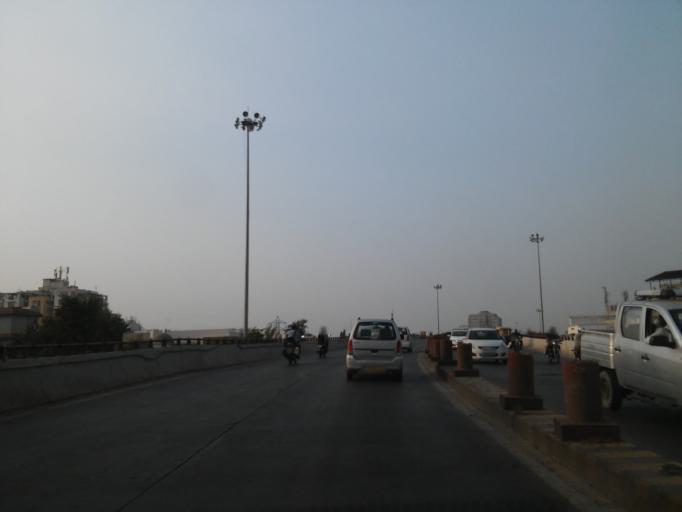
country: IN
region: Gujarat
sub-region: Ahmadabad
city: Ahmedabad
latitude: 23.0111
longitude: 72.5461
